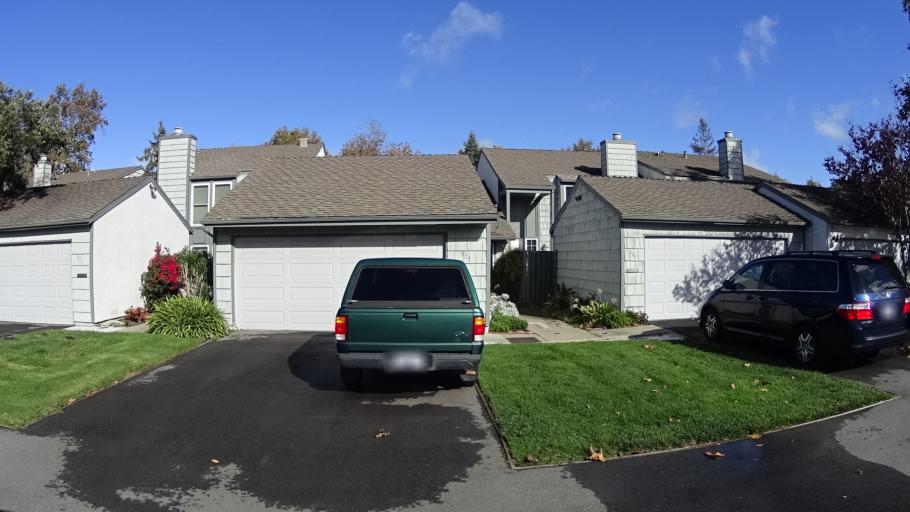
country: US
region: California
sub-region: San Mateo County
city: Foster City
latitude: 37.5498
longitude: -122.2673
